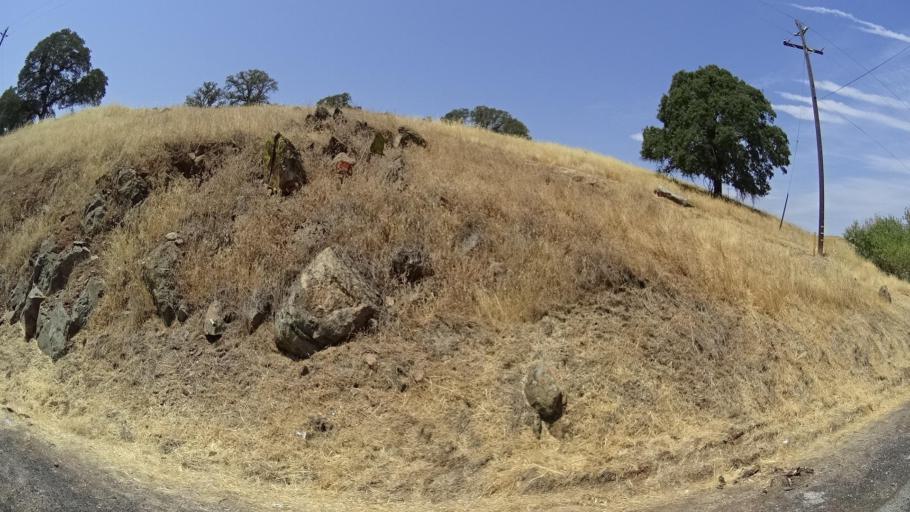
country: US
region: California
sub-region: Tuolumne County
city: Jamestown
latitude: 37.6402
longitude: -120.3434
